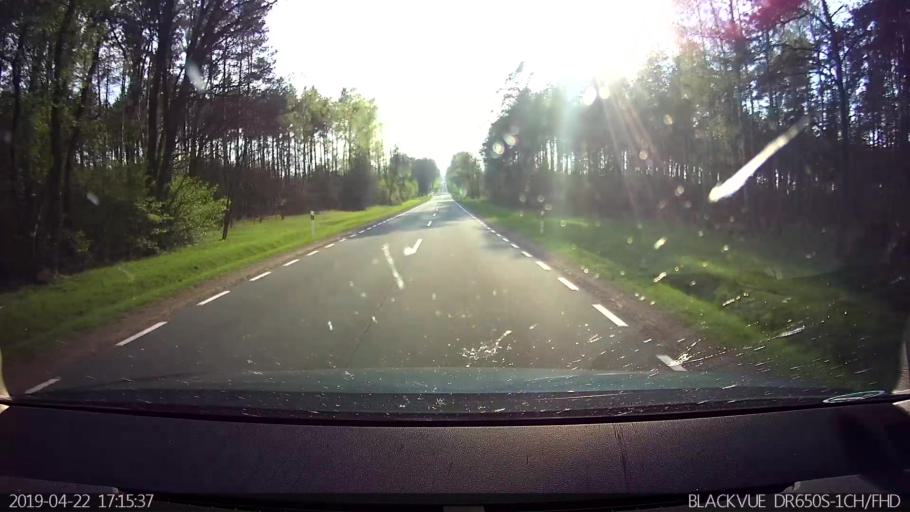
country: PL
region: Masovian Voivodeship
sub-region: Powiat sokolowski
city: Jablonna Lacka
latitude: 52.3999
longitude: 22.4826
